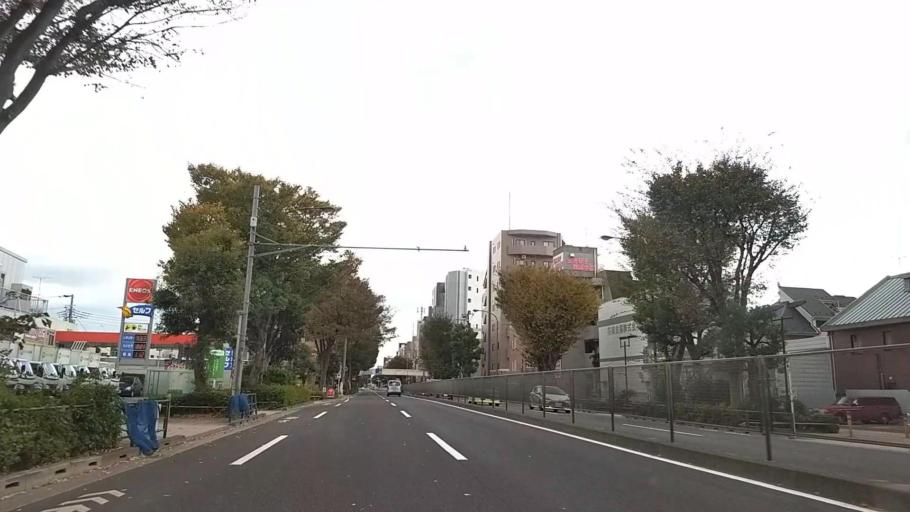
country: JP
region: Tokyo
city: Tokyo
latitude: 35.6121
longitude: 139.6887
